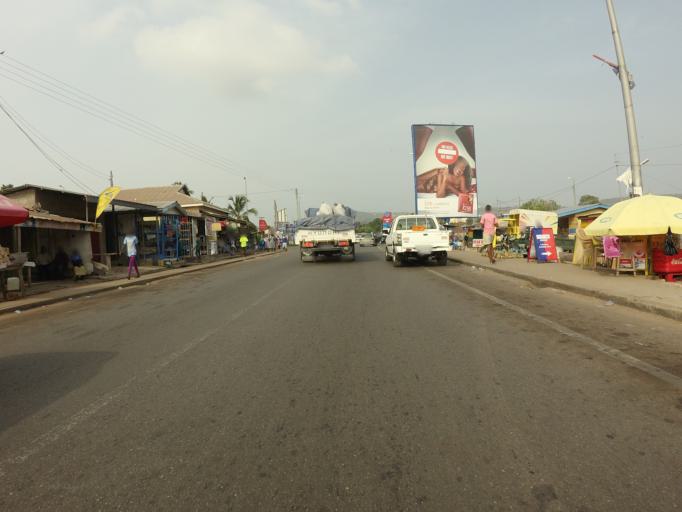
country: GH
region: Volta
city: Ho
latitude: 6.6046
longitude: 0.4756
